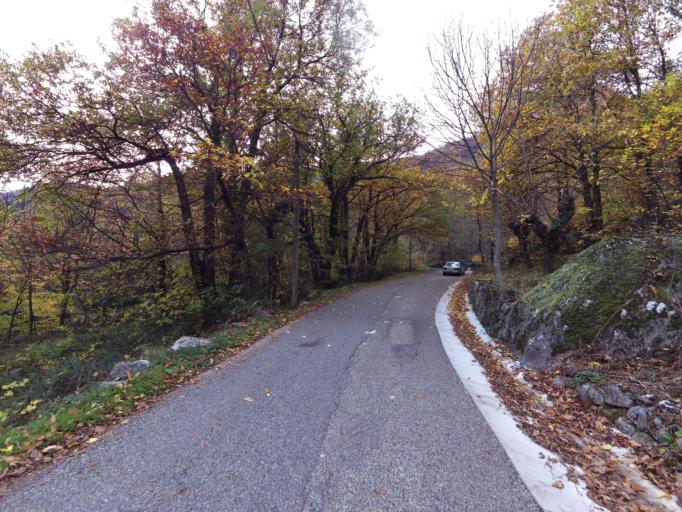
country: FR
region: Rhone-Alpes
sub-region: Departement de l'Ardeche
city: Les Vans
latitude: 44.5300
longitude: 4.0450
